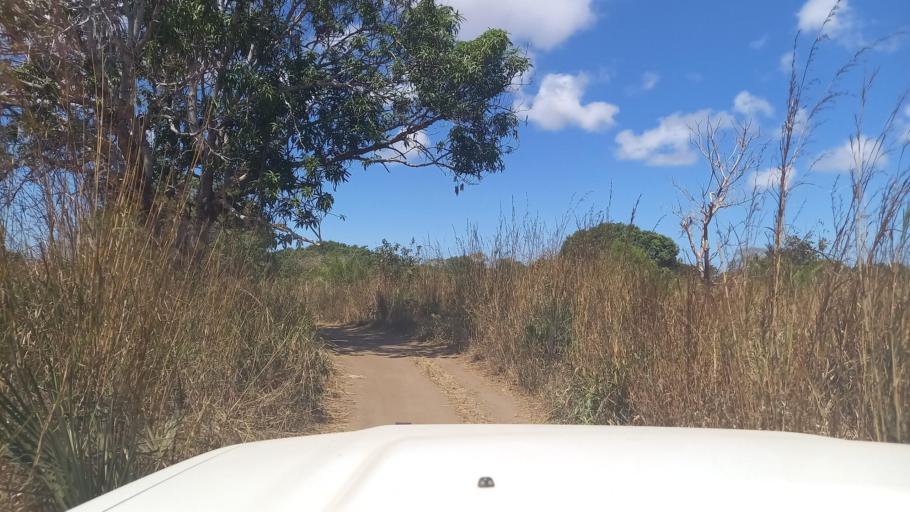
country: MZ
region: Cabo Delgado
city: Pemba
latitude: -13.4239
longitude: 40.4815
